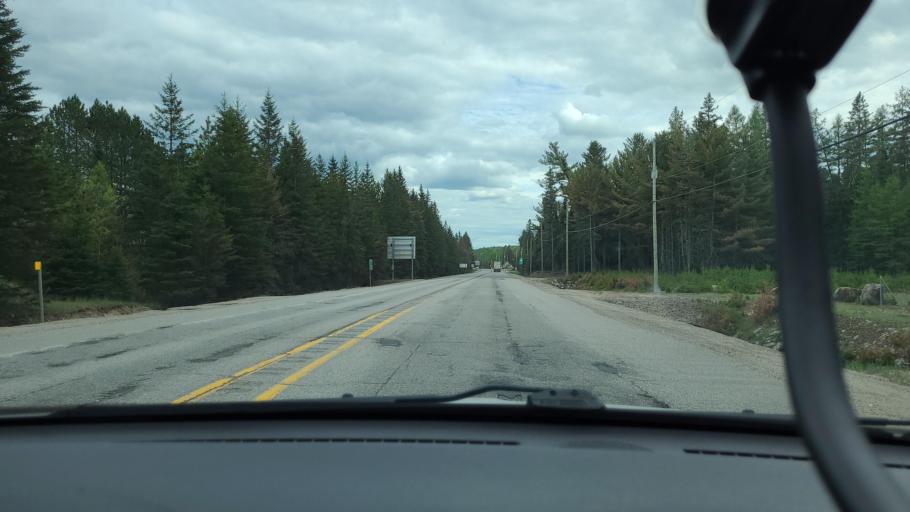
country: CA
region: Quebec
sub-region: Laurentides
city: Riviere-Rouge
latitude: 46.3875
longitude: -74.8601
